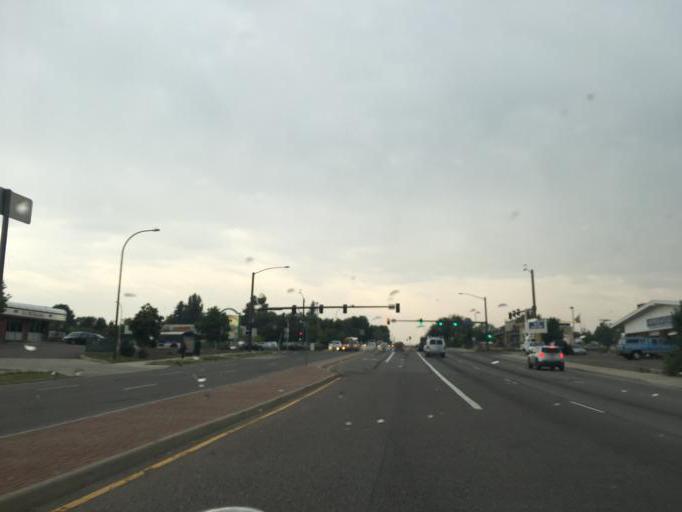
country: US
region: Colorado
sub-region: Jefferson County
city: Wheat Ridge
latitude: 39.7413
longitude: -105.1096
